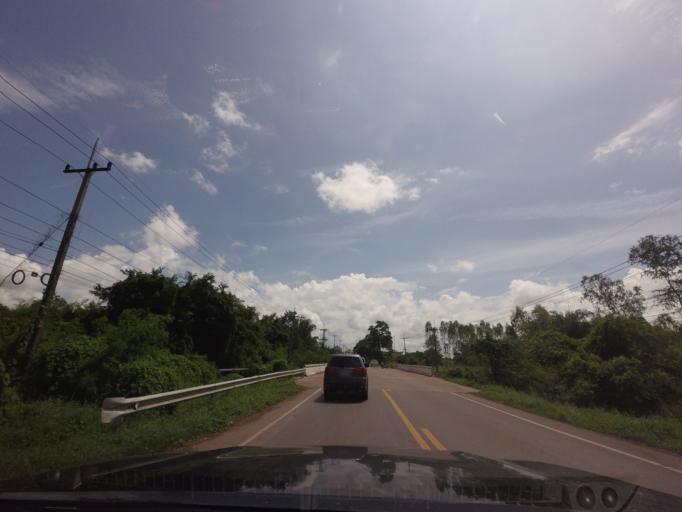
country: TH
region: Changwat Udon Thani
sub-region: Amphoe Ban Phue
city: Ban Phue
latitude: 17.6982
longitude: 102.4487
